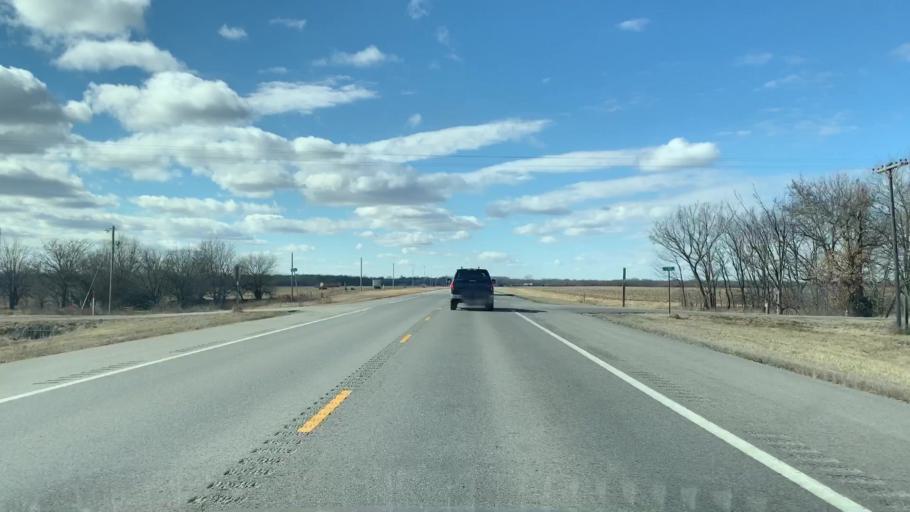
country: US
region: Kansas
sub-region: Cherokee County
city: Columbus
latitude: 37.3397
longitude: -94.8682
